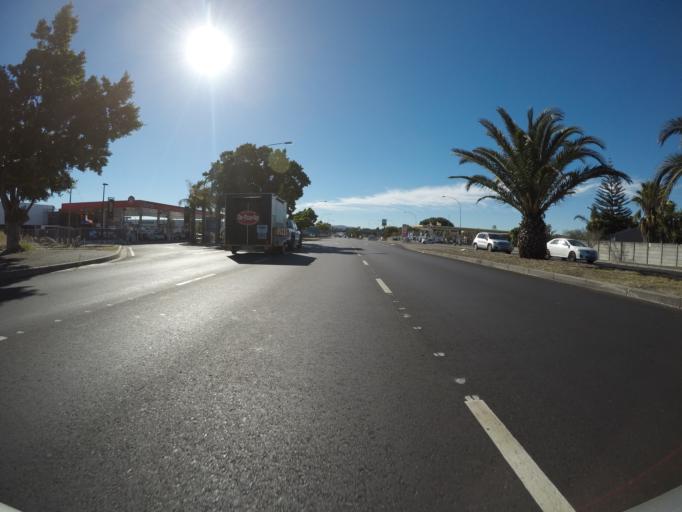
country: ZA
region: Western Cape
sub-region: City of Cape Town
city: Kraaifontein
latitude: -33.9165
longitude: 18.6716
